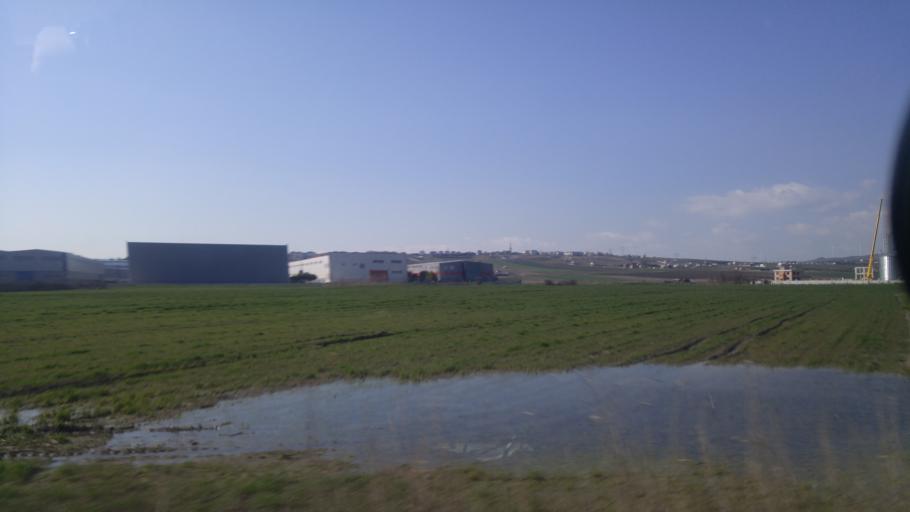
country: TR
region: Istanbul
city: Canta
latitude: 41.0783
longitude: 28.1066
